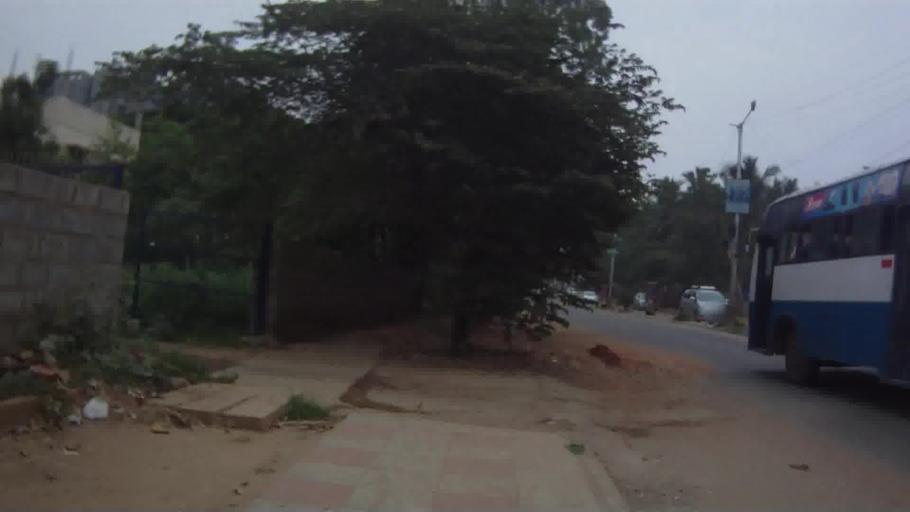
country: IN
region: Karnataka
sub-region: Bangalore Urban
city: Bangalore
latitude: 12.9559
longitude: 77.7263
